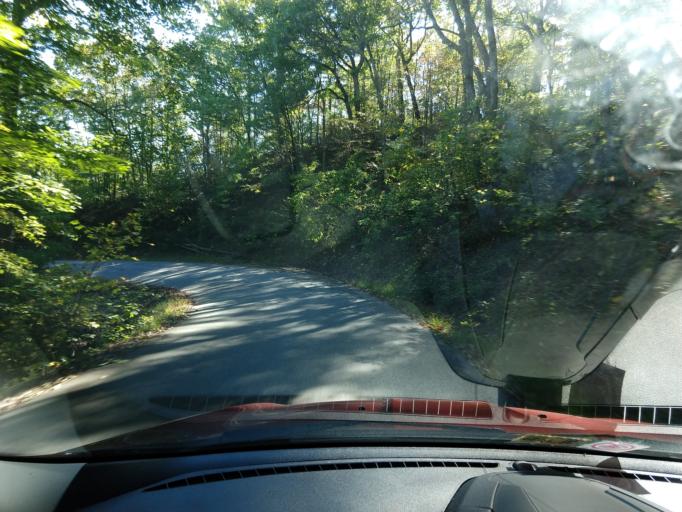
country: US
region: Virginia
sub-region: Alleghany County
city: Clifton Forge
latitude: 37.8677
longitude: -79.8823
